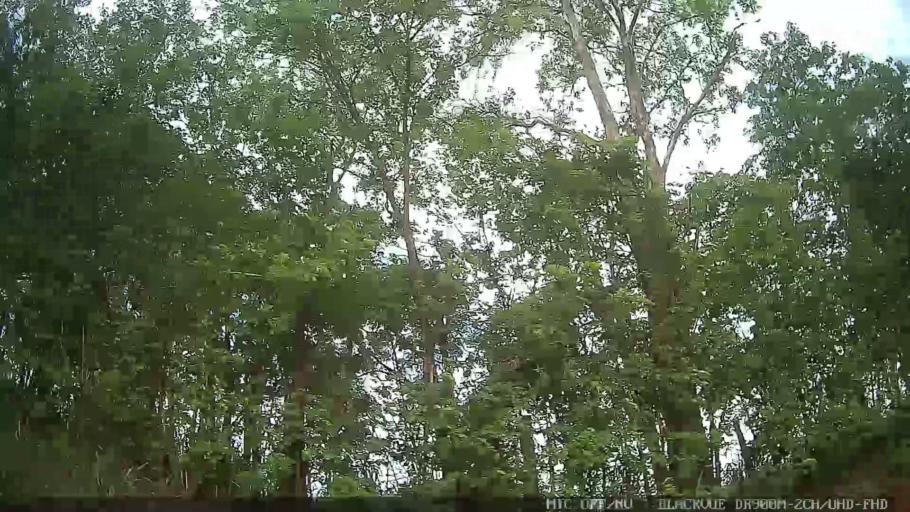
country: BR
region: Sao Paulo
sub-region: Jaguariuna
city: Jaguariuna
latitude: -22.7270
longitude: -47.0013
